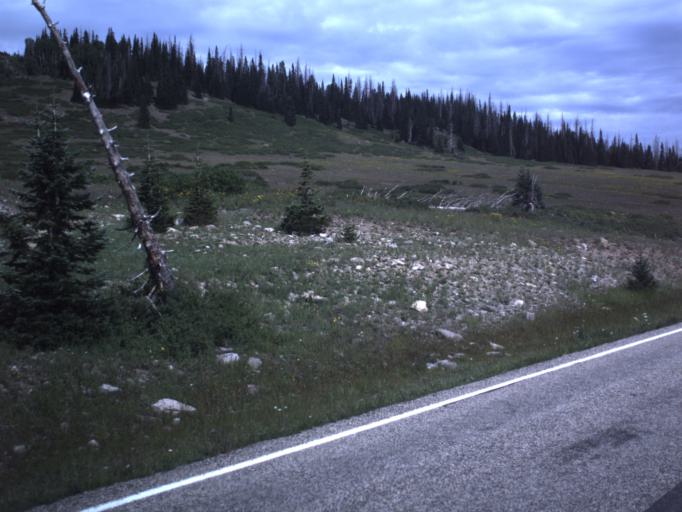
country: US
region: Utah
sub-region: Iron County
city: Cedar City
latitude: 37.6005
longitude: -112.8503
